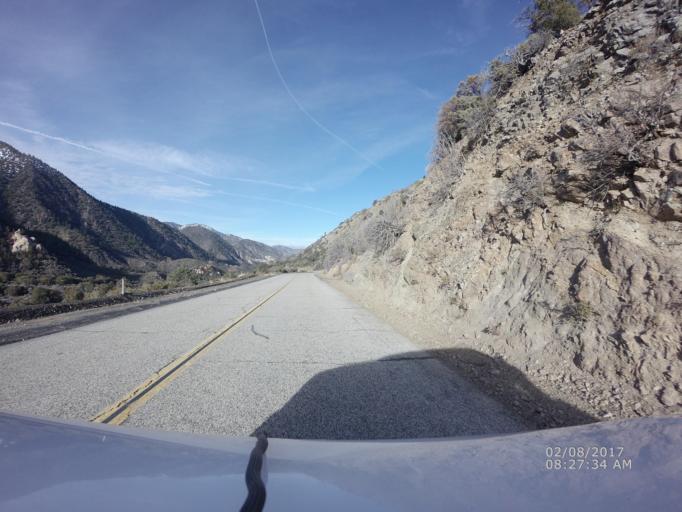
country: US
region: California
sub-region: San Bernardino County
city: Pinon Hills
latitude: 34.3943
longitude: -117.7905
